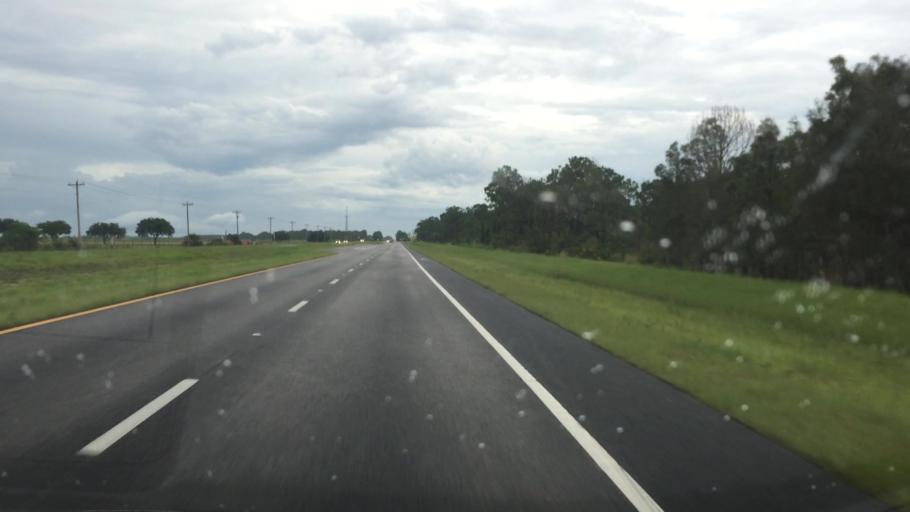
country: US
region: Florida
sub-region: Lee County
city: Lehigh Acres
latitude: 26.5157
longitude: -81.5536
